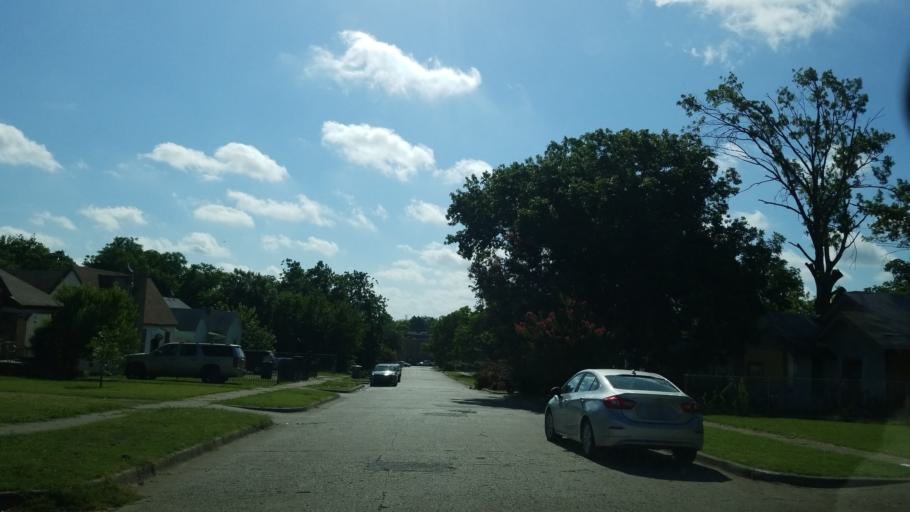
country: US
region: Texas
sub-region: Dallas County
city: Dallas
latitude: 32.7190
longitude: -96.8024
